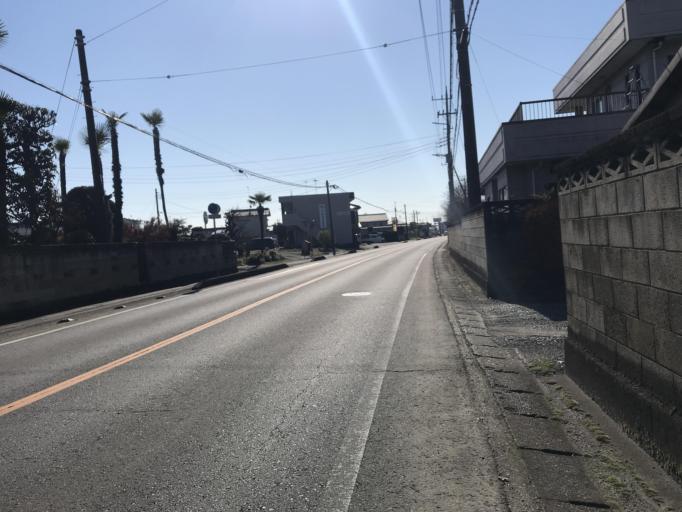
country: JP
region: Ibaraki
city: Sakai
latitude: 36.1458
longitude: 139.8118
